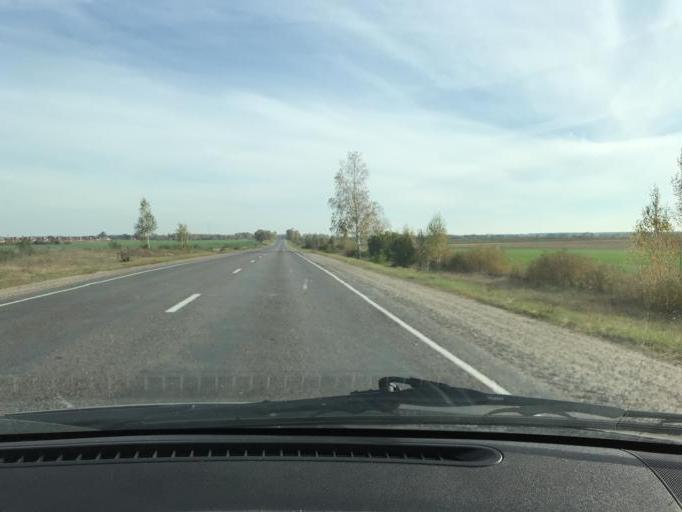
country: BY
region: Brest
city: Asnyezhytsy
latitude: 52.2093
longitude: 26.0498
